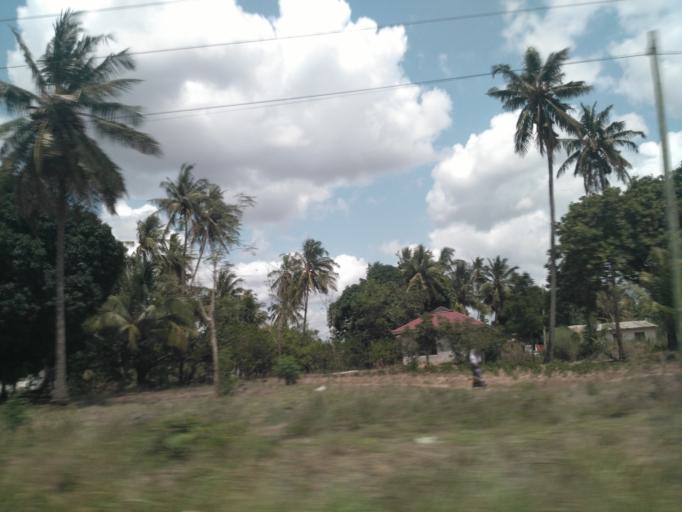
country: TZ
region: Dar es Salaam
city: Dar es Salaam
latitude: -6.8822
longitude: 39.3417
